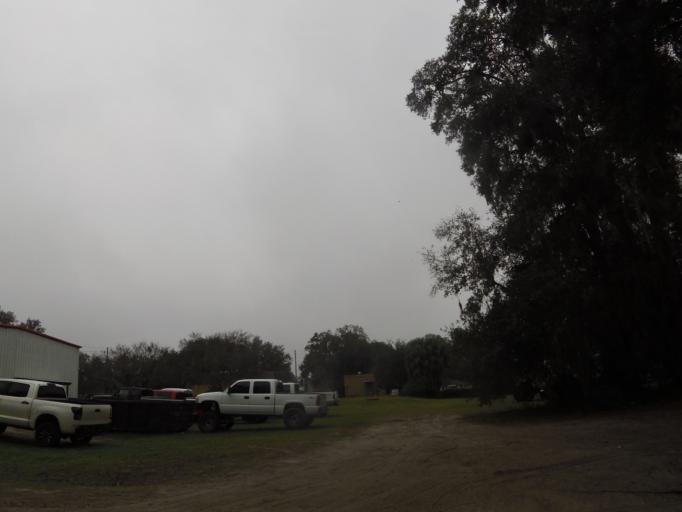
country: US
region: Florida
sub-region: Alachua County
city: High Springs
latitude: 29.8316
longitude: -82.5950
